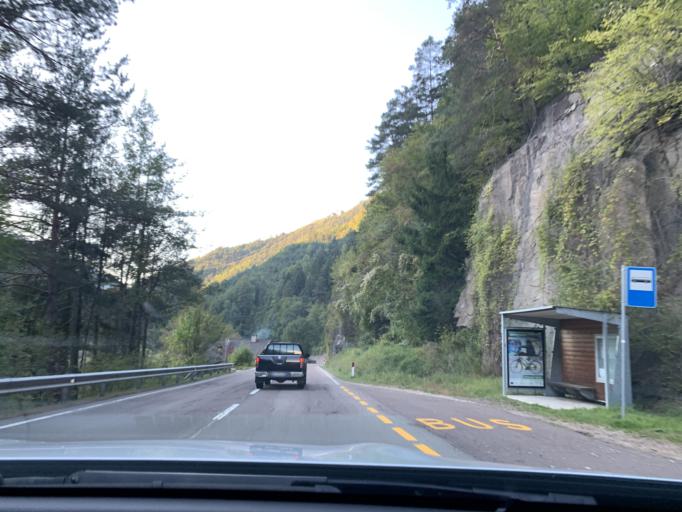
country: IT
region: Trentino-Alto Adige
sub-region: Bolzano
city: Nova Ponente
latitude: 46.4496
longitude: 11.4488
